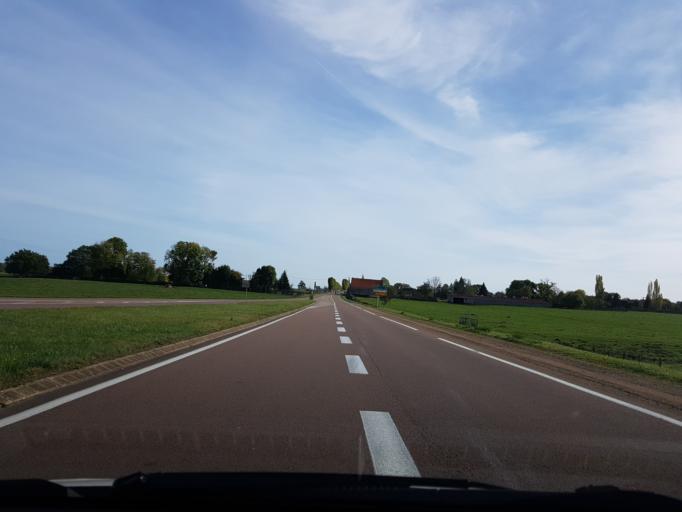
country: FR
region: Bourgogne
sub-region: Departement de l'Yonne
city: Avallon
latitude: 47.4855
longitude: 3.9917
